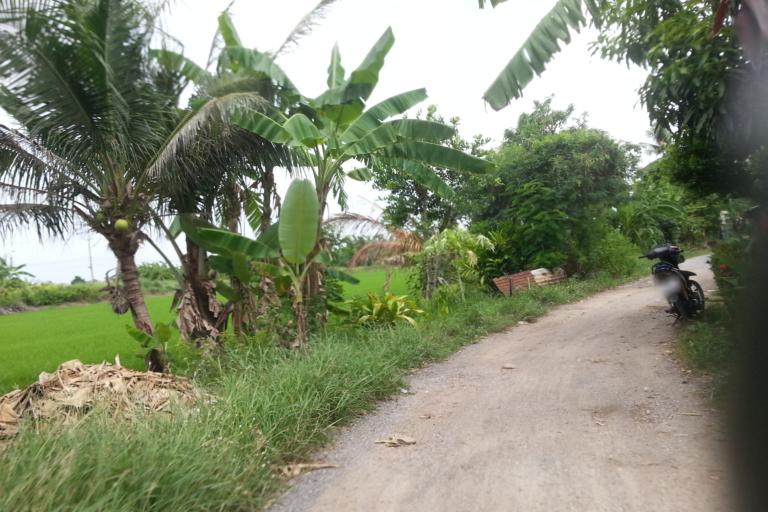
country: TH
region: Pathum Thani
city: Ban Rangsit
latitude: 14.0489
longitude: 100.8240
